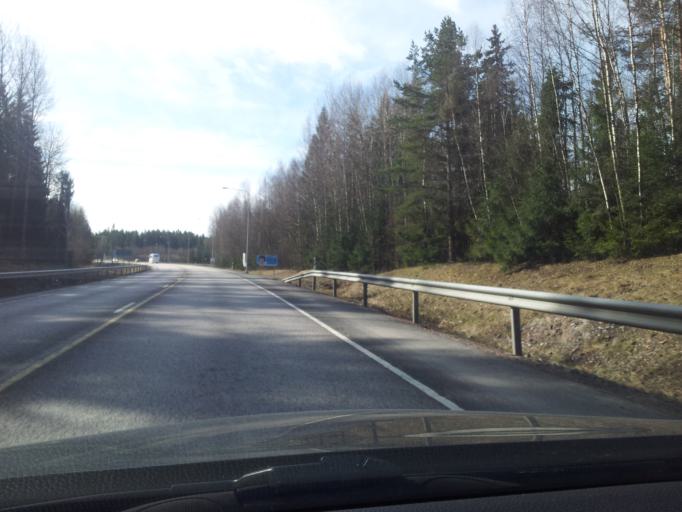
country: FI
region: Uusimaa
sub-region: Helsinki
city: Kirkkonummi
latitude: 60.1442
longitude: 24.5372
